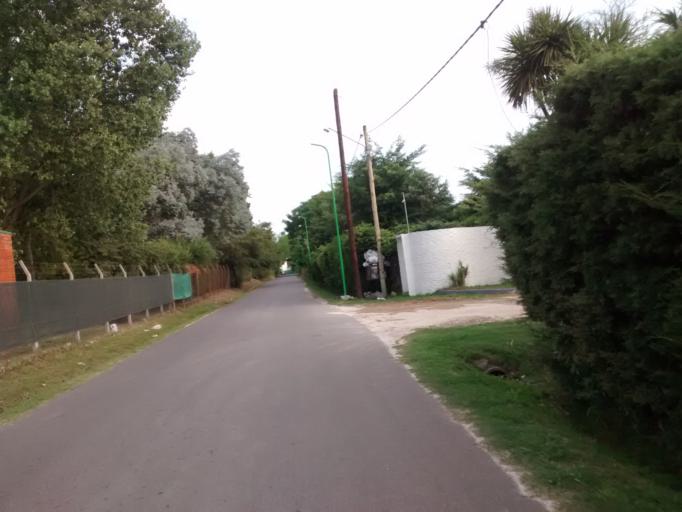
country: AR
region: Buenos Aires
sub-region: Partido de La Plata
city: La Plata
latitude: -34.8472
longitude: -58.0953
